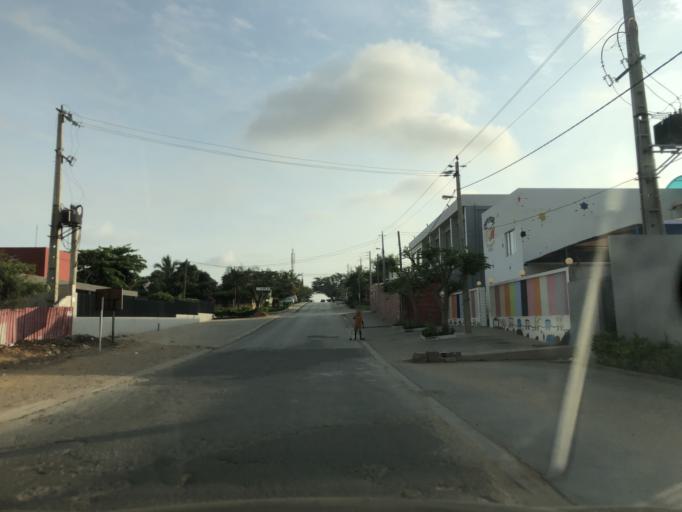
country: AO
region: Luanda
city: Luanda
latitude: -8.9011
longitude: 13.2262
